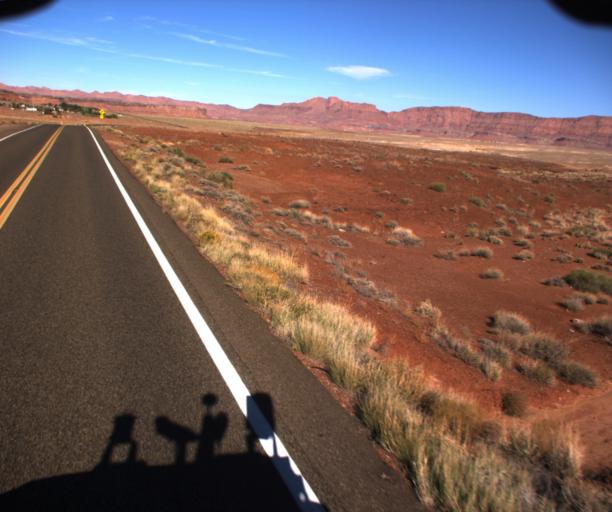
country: US
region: Arizona
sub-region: Coconino County
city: Page
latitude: 36.7762
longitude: -111.6964
